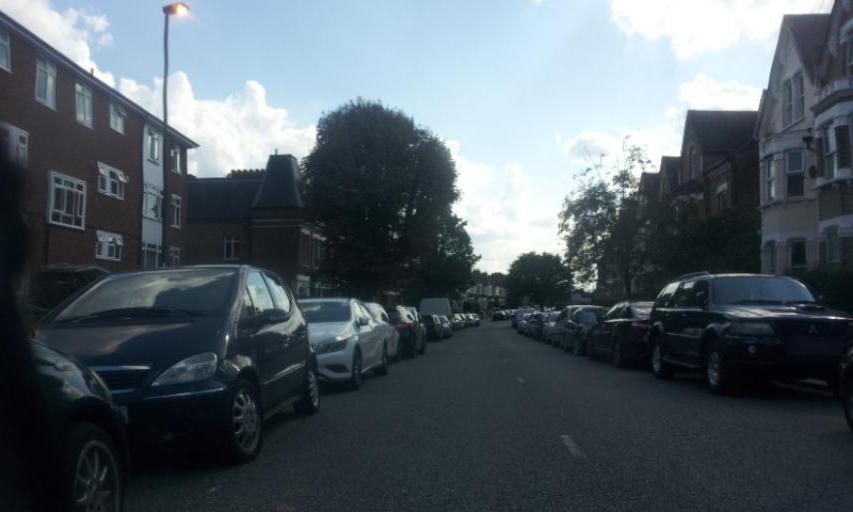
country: GB
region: England
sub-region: Greater London
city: Beckenham
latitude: 51.4246
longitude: -0.0545
